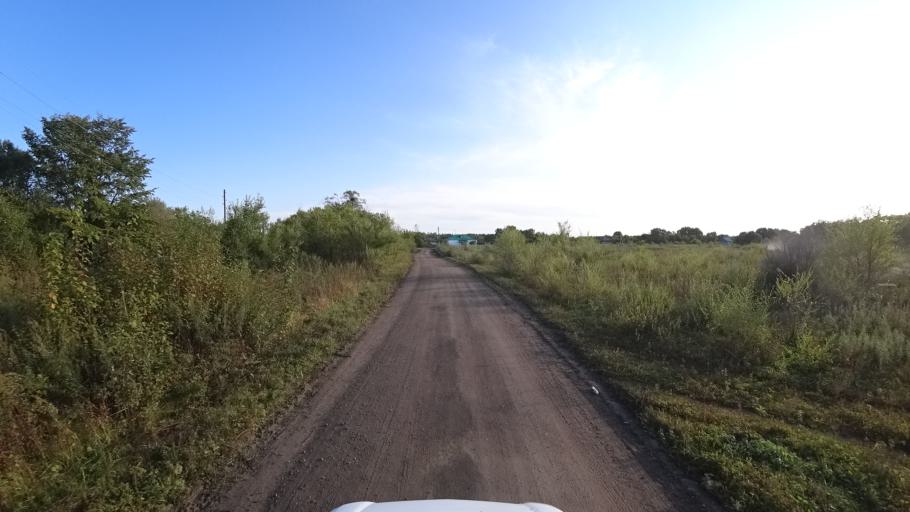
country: RU
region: Amur
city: Arkhara
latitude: 49.3543
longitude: 130.1100
